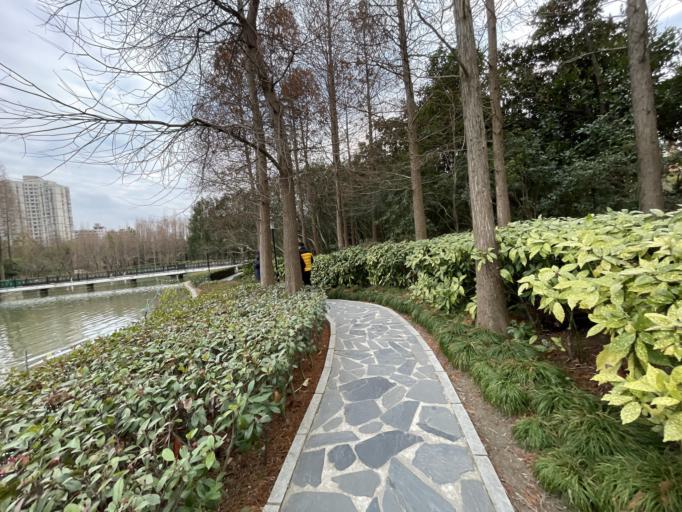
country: CN
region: Shanghai Shi
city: Yangpu
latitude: 31.2936
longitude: 121.5234
